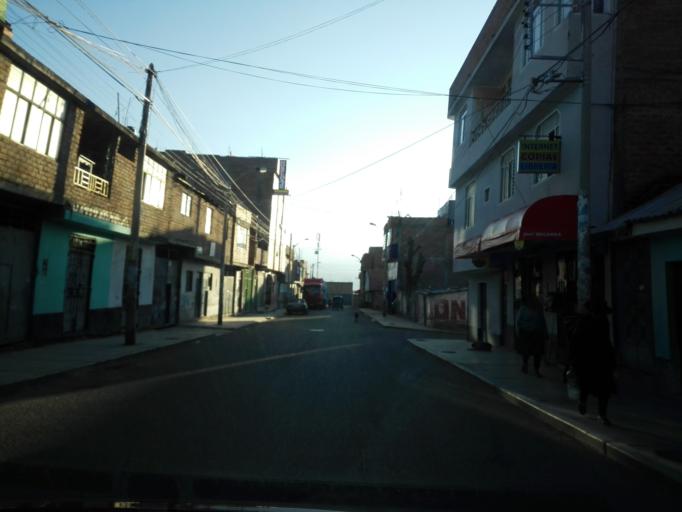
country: PE
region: Ayacucho
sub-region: Provincia de Huamanga
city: Ayacucho
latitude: -13.1500
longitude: -74.2148
